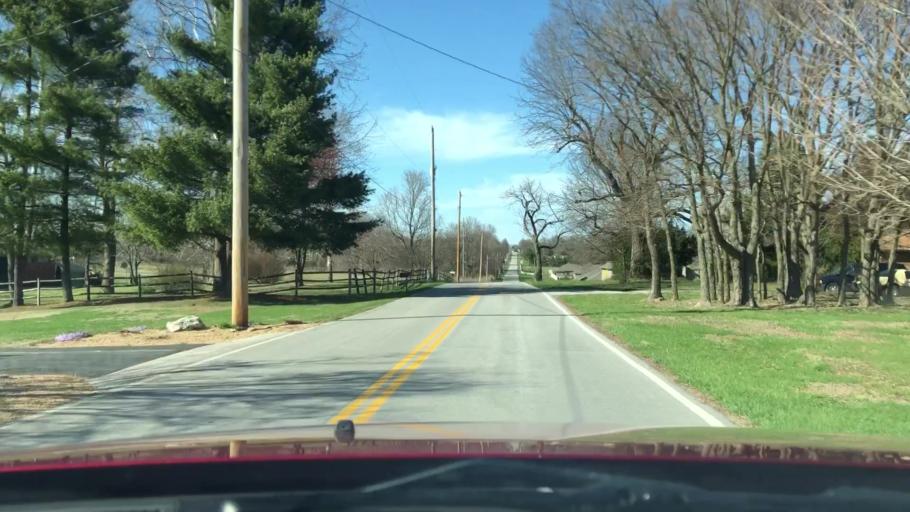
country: US
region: Missouri
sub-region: Greene County
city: Strafford
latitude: 37.2276
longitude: -93.1884
